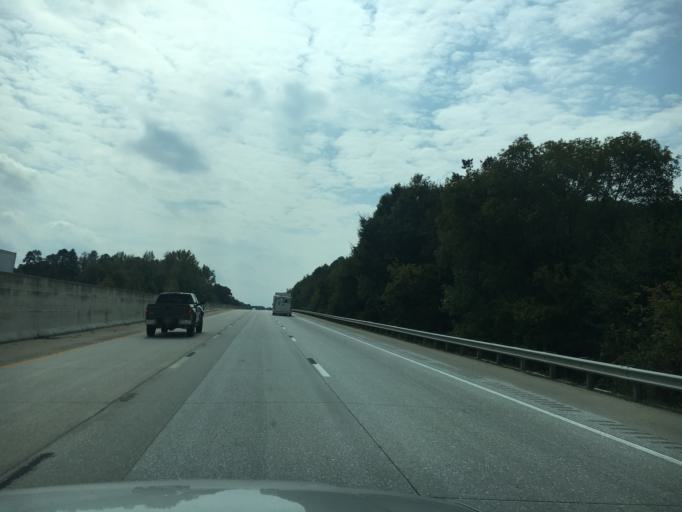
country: US
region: South Carolina
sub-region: Anderson County
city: Northlake
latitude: 34.6187
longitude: -82.6201
